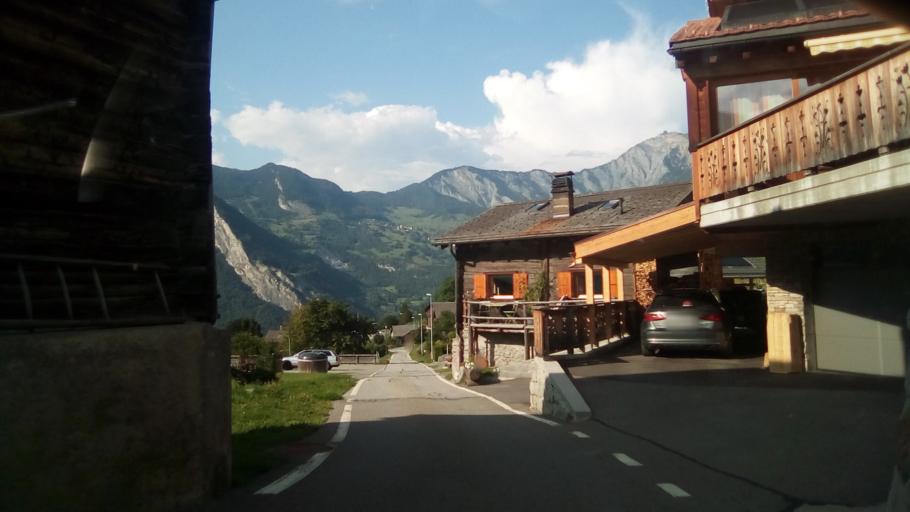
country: CH
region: Valais
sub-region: Entremont District
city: Orsieres
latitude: 46.0598
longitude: 7.1546
